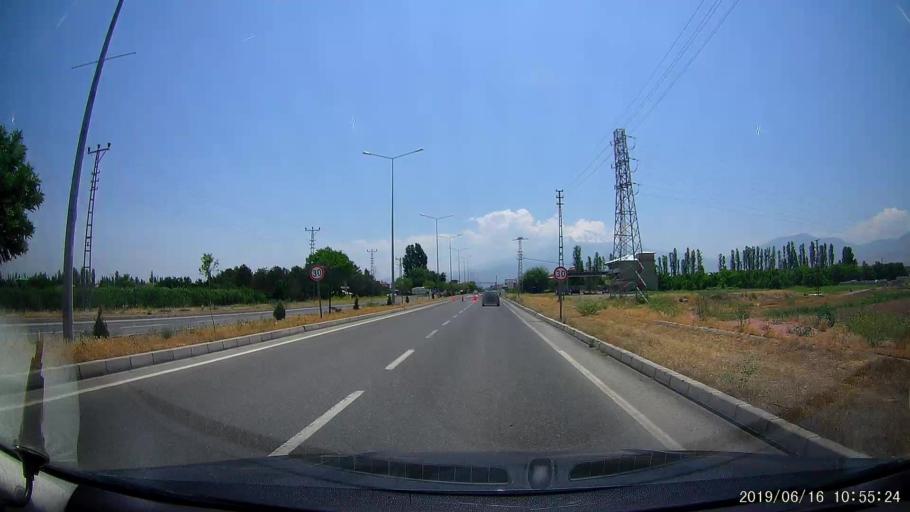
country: TR
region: Igdir
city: Igdir
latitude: 39.9363
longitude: 44.0101
